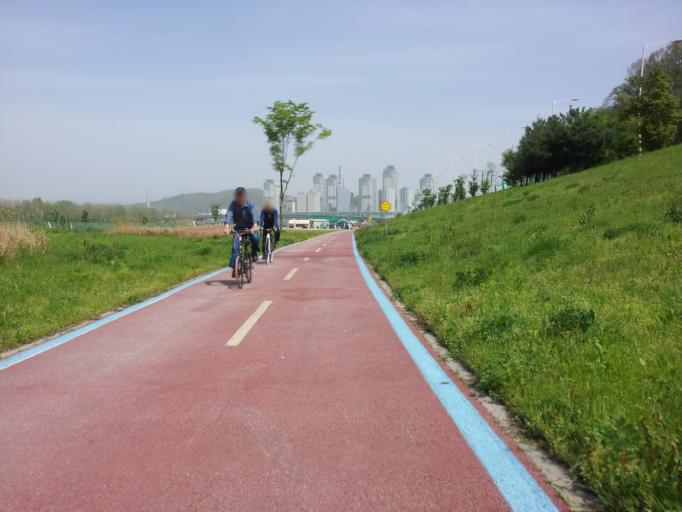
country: KR
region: Daejeon
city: Daejeon
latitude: 36.3647
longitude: 127.3978
